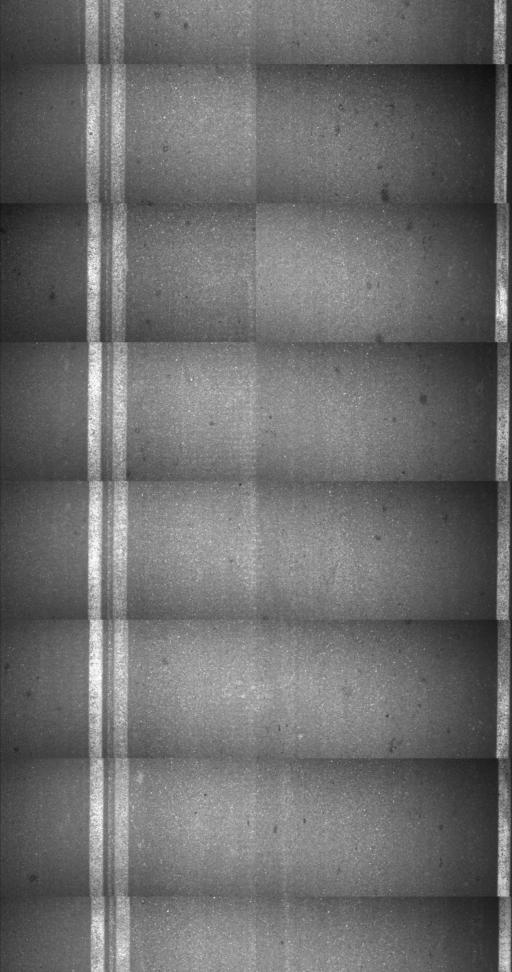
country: US
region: New Hampshire
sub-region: Coos County
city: Colebrook
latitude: 44.9603
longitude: -71.5277
